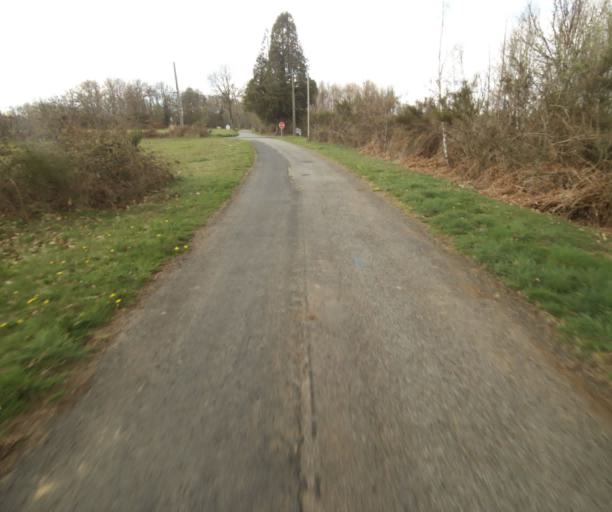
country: FR
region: Limousin
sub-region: Departement de la Correze
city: Egletons
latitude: 45.2606
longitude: 1.9920
